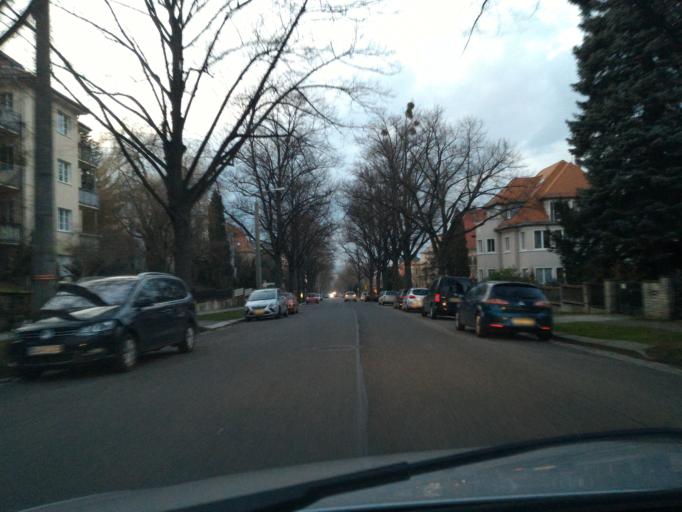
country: DE
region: Saxony
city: Bannewitz
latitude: 51.0236
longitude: 13.7152
